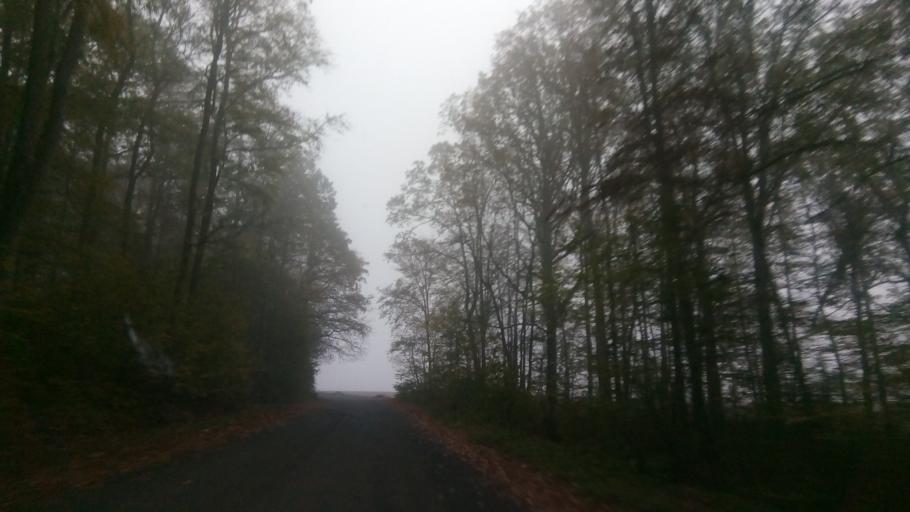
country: DE
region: Bavaria
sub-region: Regierungsbezirk Unterfranken
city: Dittelbrunn
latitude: 50.0899
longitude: 10.2372
